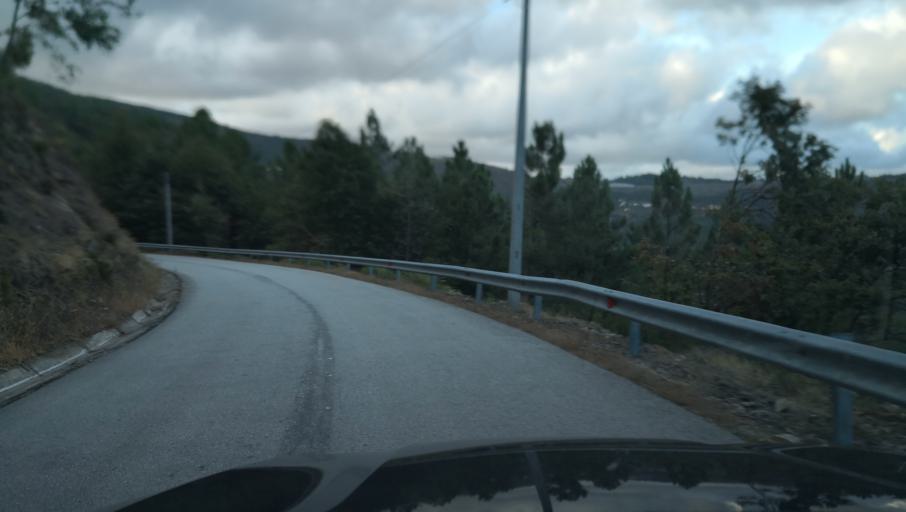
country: PT
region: Vila Real
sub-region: Santa Marta de Penaguiao
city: Santa Marta de Penaguiao
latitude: 41.2536
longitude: -7.8537
